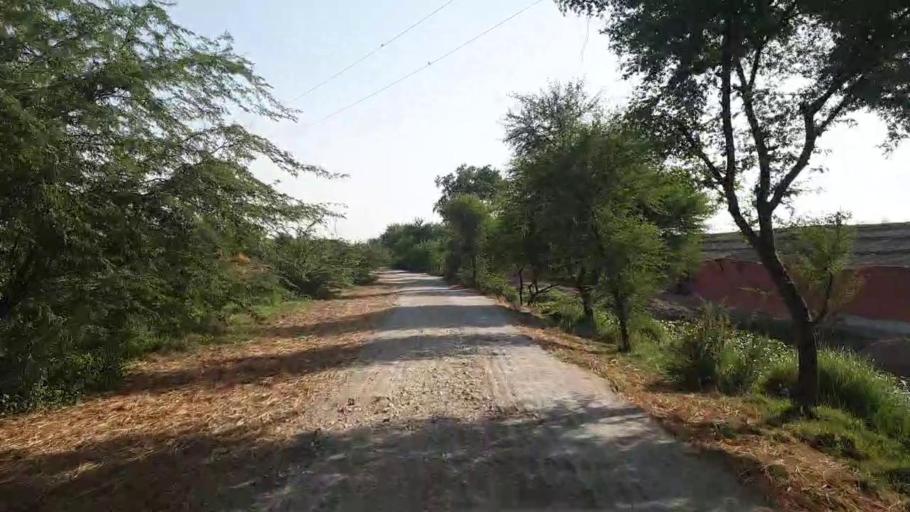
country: PK
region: Sindh
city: Matli
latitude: 25.0290
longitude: 68.7321
